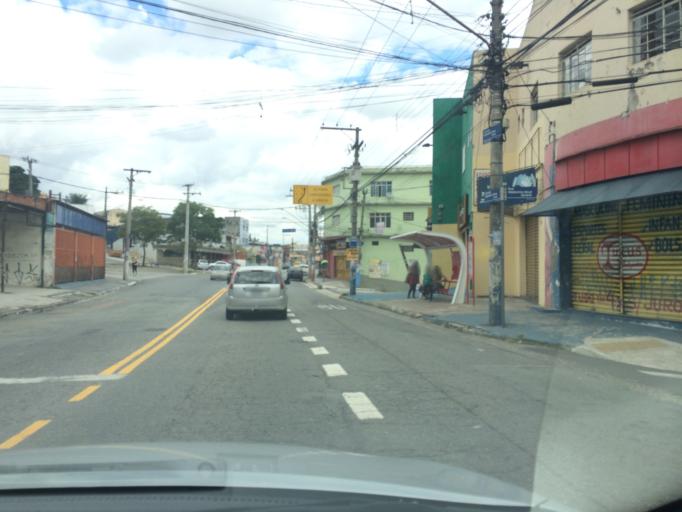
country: BR
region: Sao Paulo
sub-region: Guarulhos
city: Guarulhos
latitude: -23.4503
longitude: -46.5207
